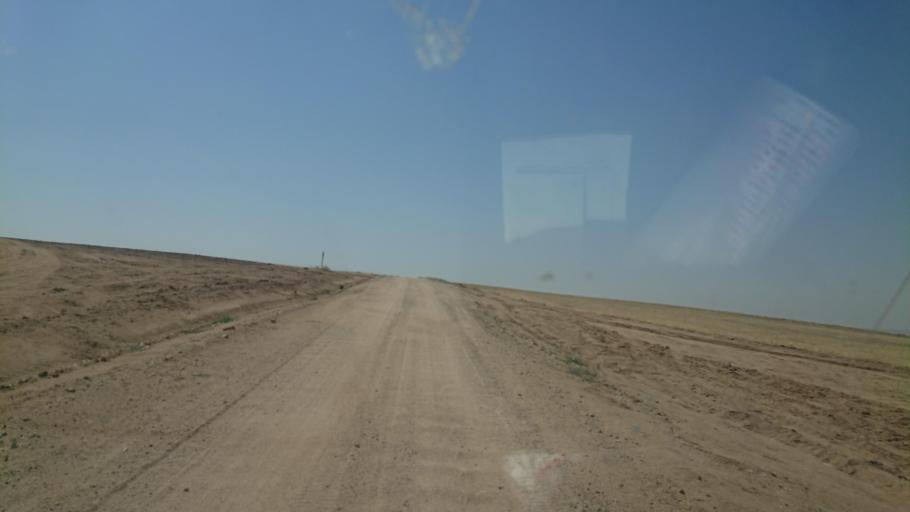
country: TR
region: Aksaray
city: Agacoren
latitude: 38.8000
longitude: 33.9443
